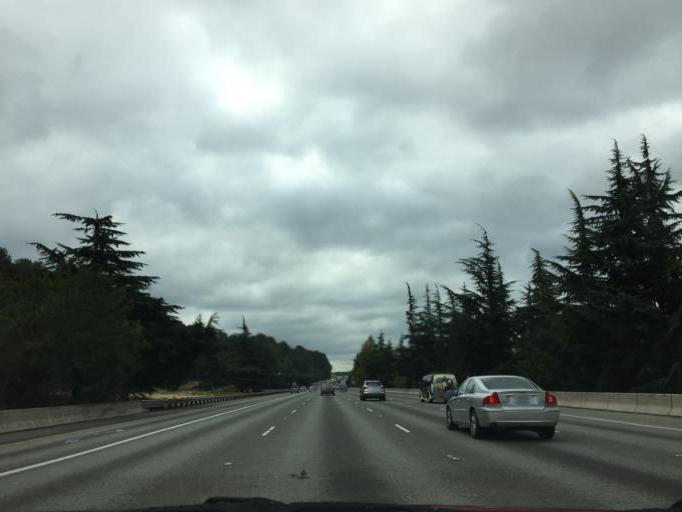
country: US
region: Washington
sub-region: King County
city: Boulevard Park
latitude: 47.5305
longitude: -122.2946
